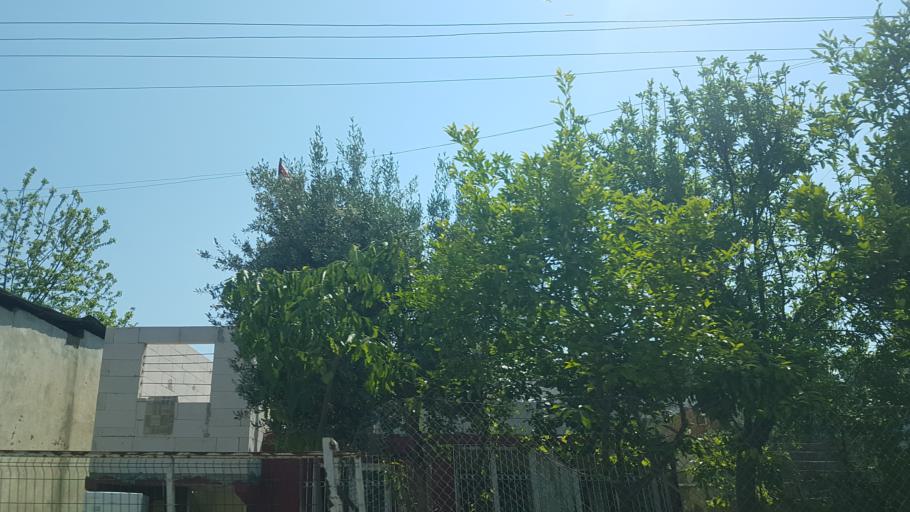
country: TR
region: Adana
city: Adana
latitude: 37.0245
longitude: 35.3655
